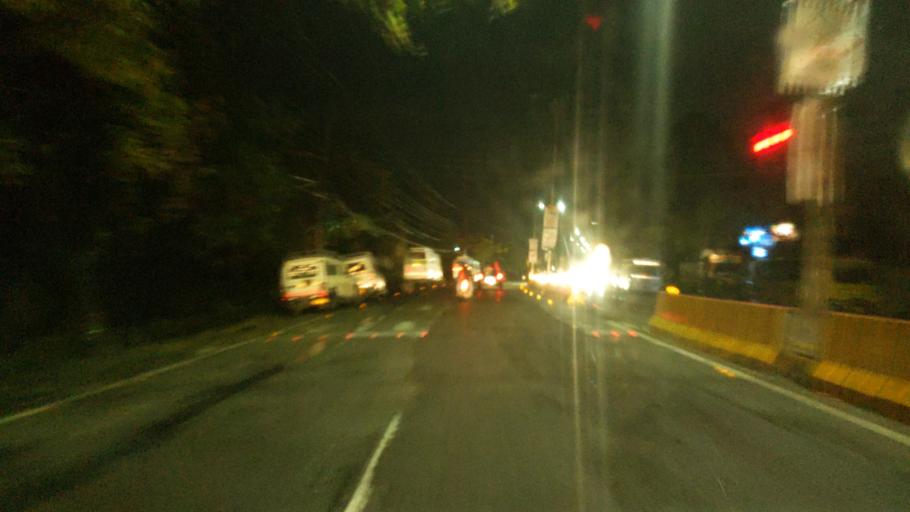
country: IN
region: Uttarakhand
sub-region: Naini Tal
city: Haldwani
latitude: 29.2571
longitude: 79.5429
